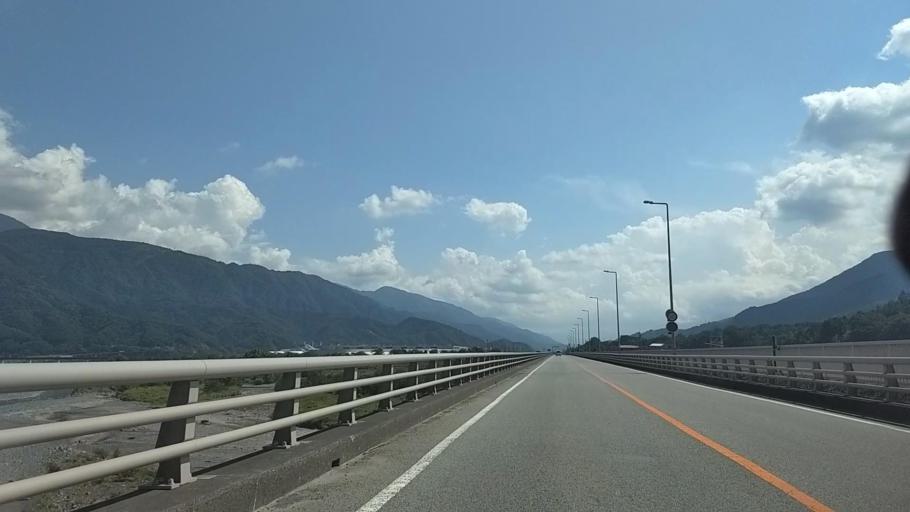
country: JP
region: Yamanashi
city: Ryuo
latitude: 35.4294
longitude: 138.4437
